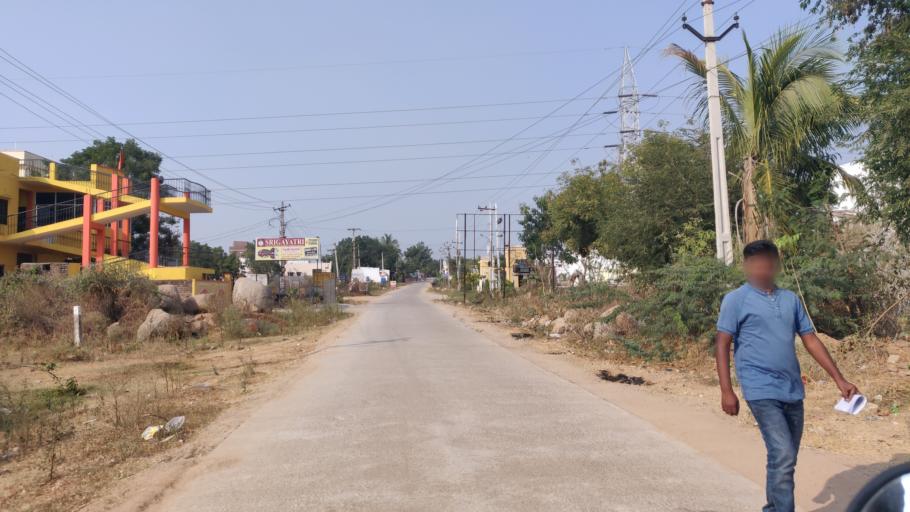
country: IN
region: Telangana
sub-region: Rangareddi
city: Uppal Kalan
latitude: 17.3961
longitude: 78.6050
